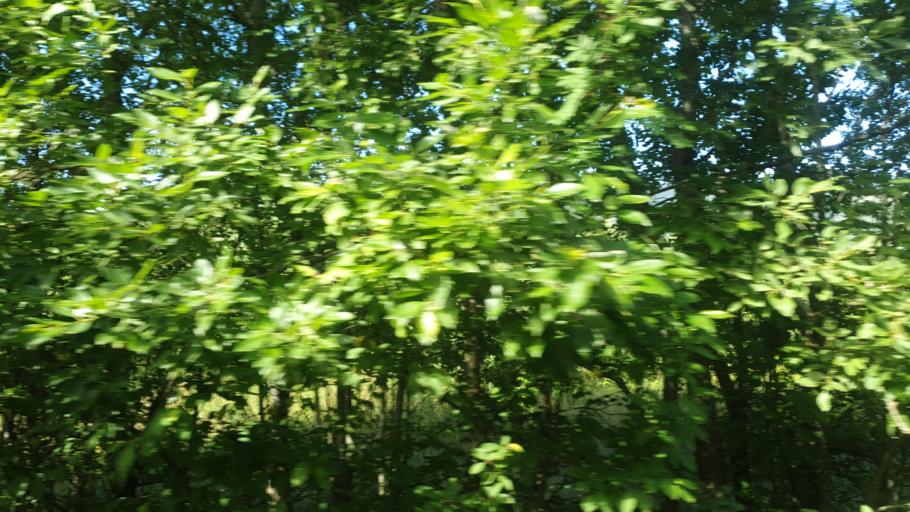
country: NO
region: Sor-Trondelag
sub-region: Orkdal
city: Orkanger
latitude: 63.2729
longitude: 9.8211
